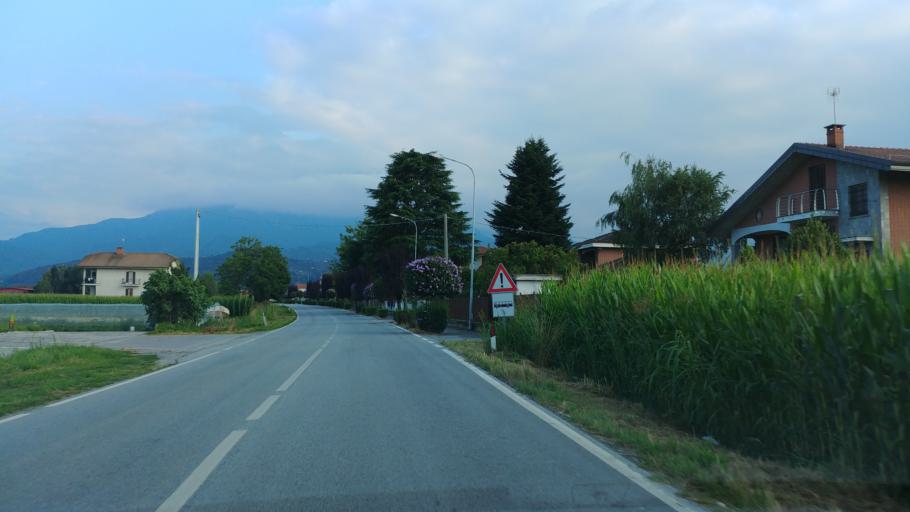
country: IT
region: Piedmont
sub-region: Provincia di Cuneo
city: Peveragno
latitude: 44.3549
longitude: 7.5913
